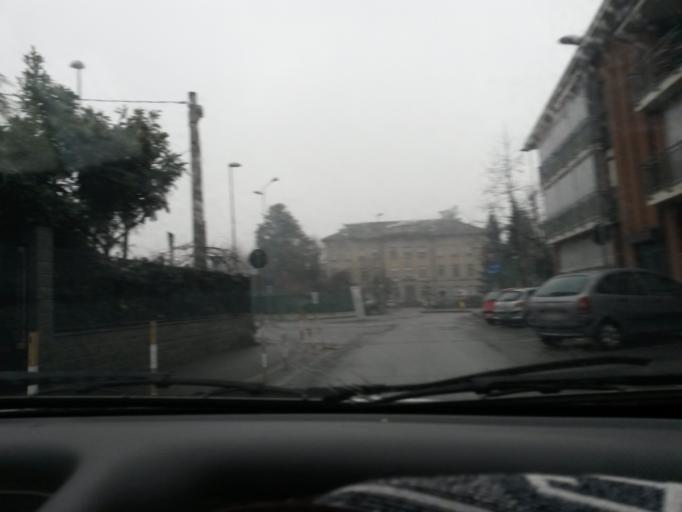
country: IT
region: Piedmont
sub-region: Provincia di Torino
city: Grugliasco
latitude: 45.0711
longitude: 7.5894
